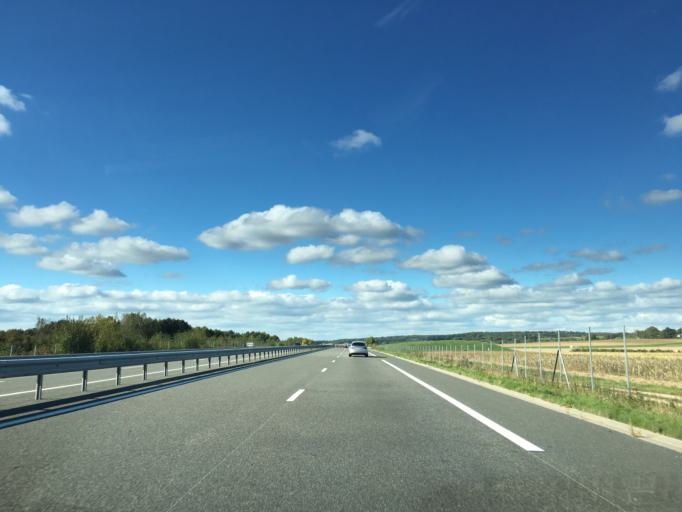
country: FR
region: Lorraine
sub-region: Departement de Meurthe-et-Moselle
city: Baccarat
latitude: 48.4752
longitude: 6.7214
